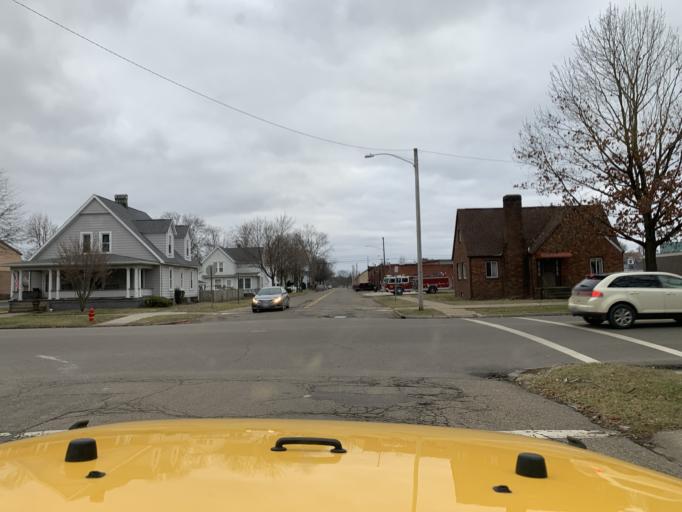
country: US
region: Ohio
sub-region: Tuscarawas County
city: Dover
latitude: 40.5235
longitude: -81.4754
